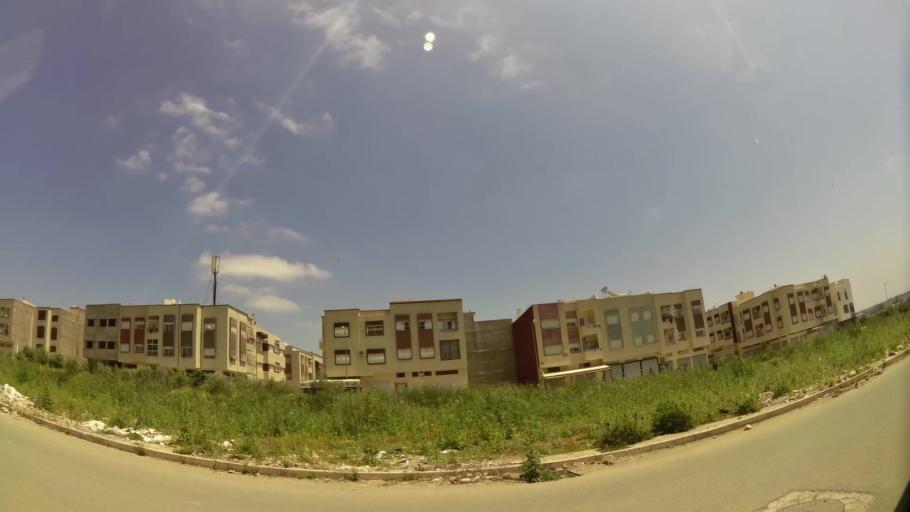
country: MA
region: Fes-Boulemane
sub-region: Fes
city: Fes
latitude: 34.0494
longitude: -5.0444
